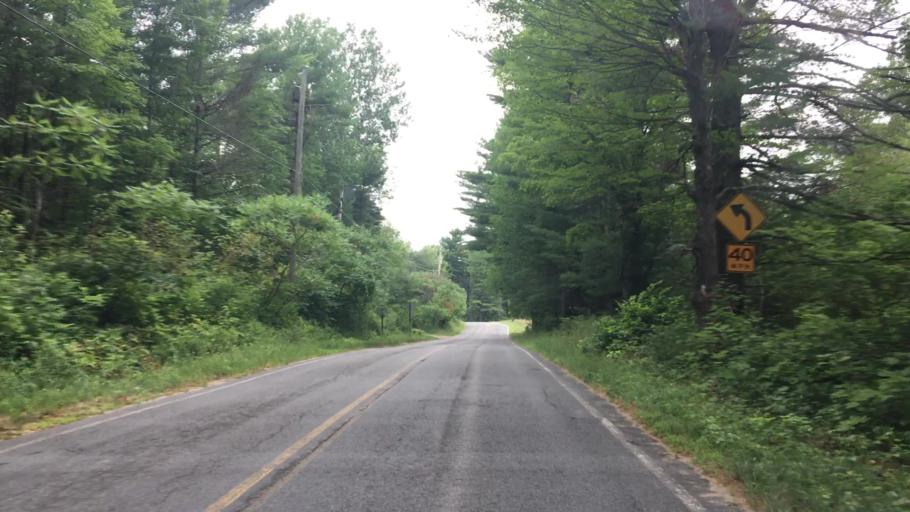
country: US
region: New York
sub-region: Essex County
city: Keeseville
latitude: 44.4368
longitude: -73.6191
